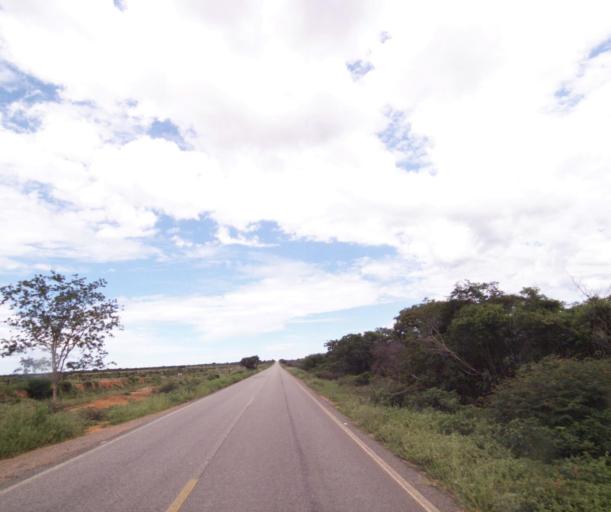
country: BR
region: Bahia
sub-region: Palmas De Monte Alto
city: Palmas de Monte Alto
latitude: -14.2570
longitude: -43.2545
